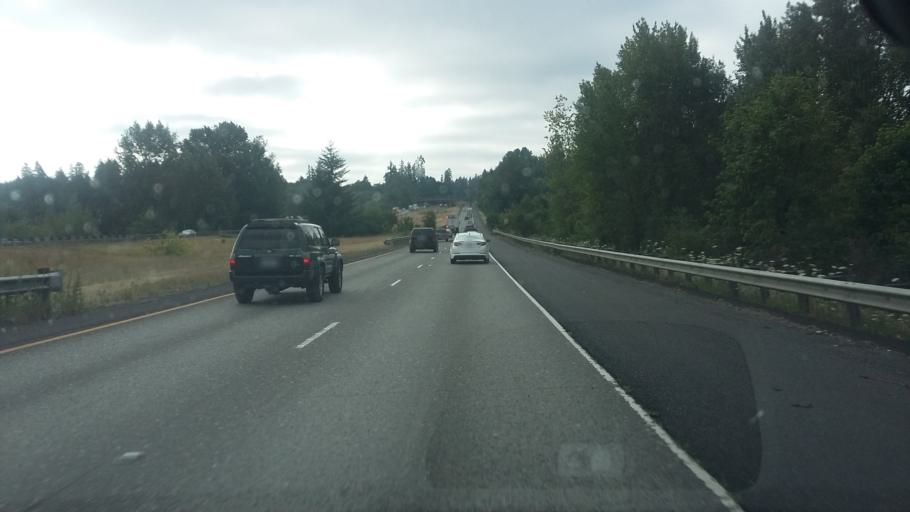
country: US
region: Washington
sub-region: Clark County
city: Salmon Creek
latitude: 45.7121
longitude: -122.6405
